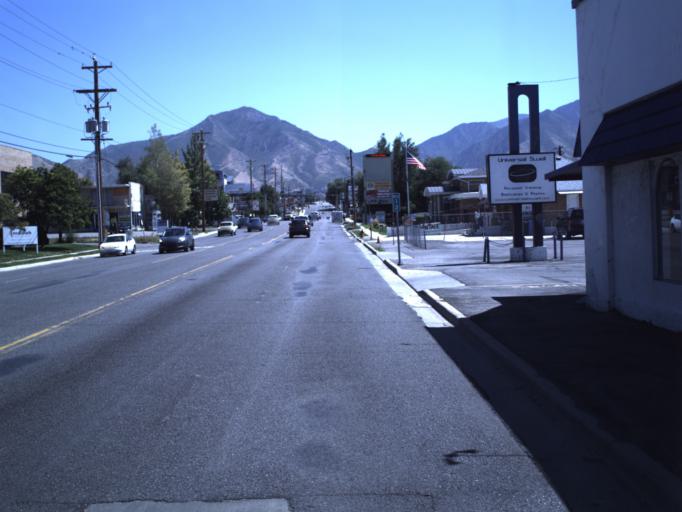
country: US
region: Utah
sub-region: Salt Lake County
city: Millcreek
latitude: 40.6998
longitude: -111.8650
